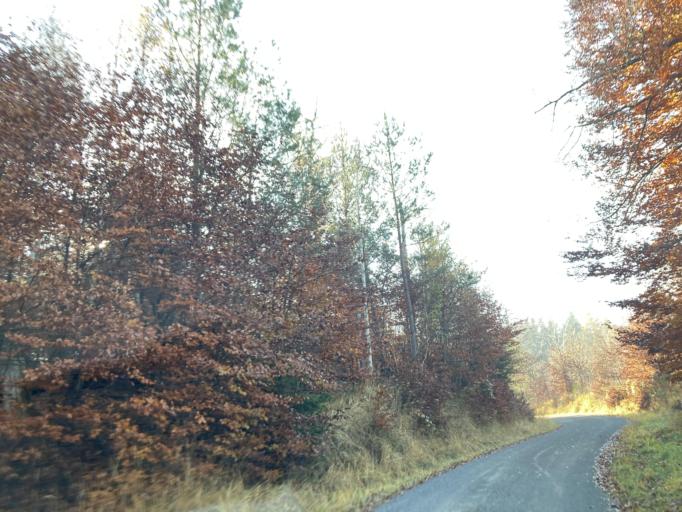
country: DE
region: Baden-Wuerttemberg
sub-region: Regierungsbezirk Stuttgart
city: Hildrizhausen
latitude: 48.5763
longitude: 8.9812
